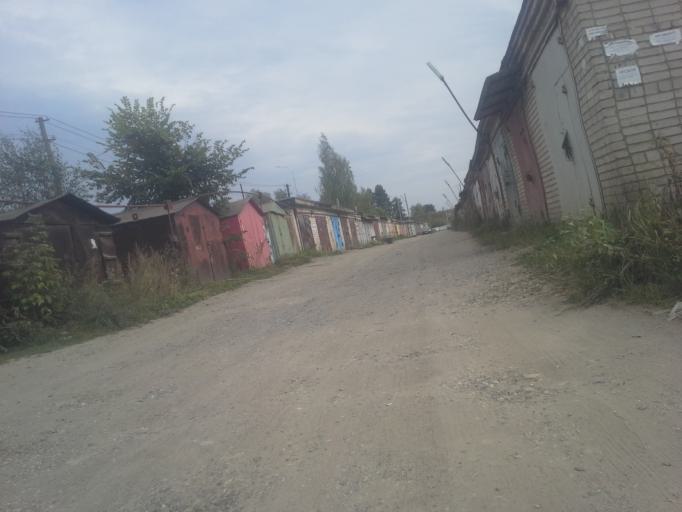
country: RU
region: Moskovskaya
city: Kievskij
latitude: 55.4242
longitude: 36.8706
